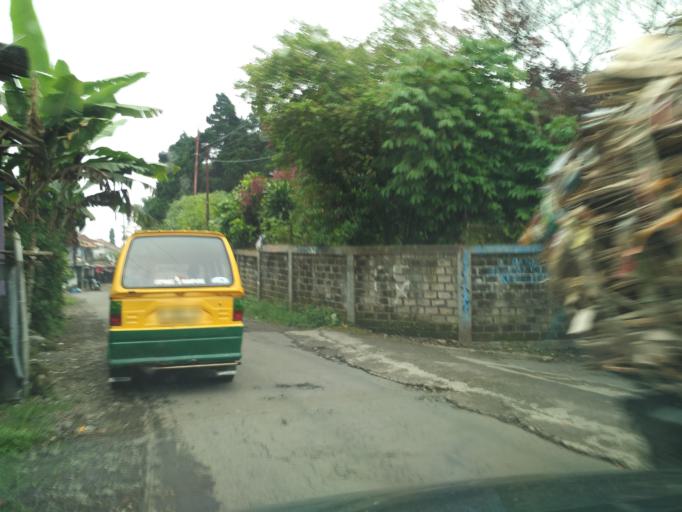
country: ID
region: West Java
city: Sukabumi
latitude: -6.7464
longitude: 107.0378
